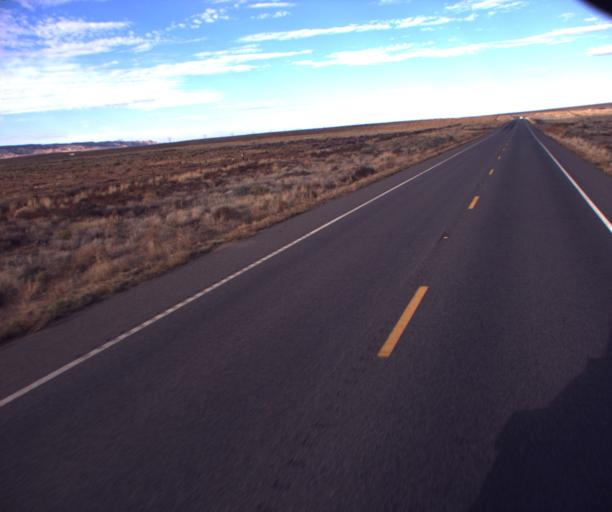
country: US
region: Arizona
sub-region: Apache County
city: Lukachukai
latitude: 36.9526
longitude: -109.2896
